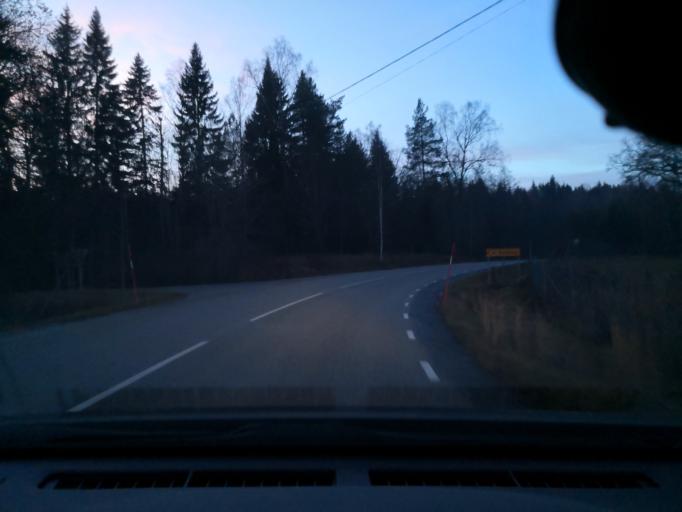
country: SE
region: OErebro
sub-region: Lindesbergs Kommun
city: Fellingsbro
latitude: 59.4006
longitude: 15.5190
